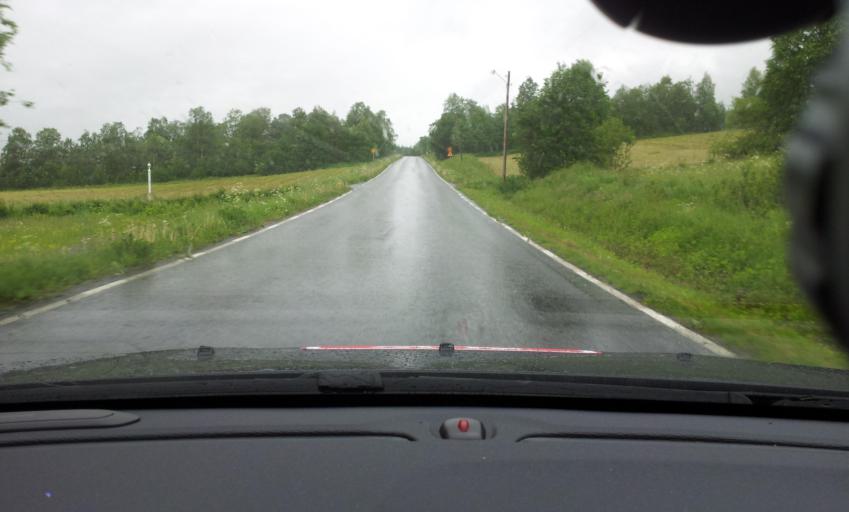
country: SE
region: Jaemtland
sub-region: Are Kommun
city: Are
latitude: 63.3131
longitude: 13.2006
